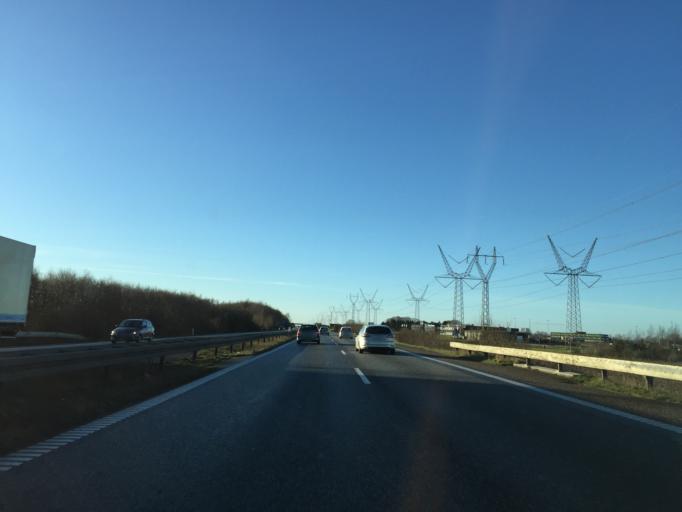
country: DK
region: South Denmark
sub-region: Odense Kommune
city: Neder Holluf
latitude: 55.3626
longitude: 10.5013
